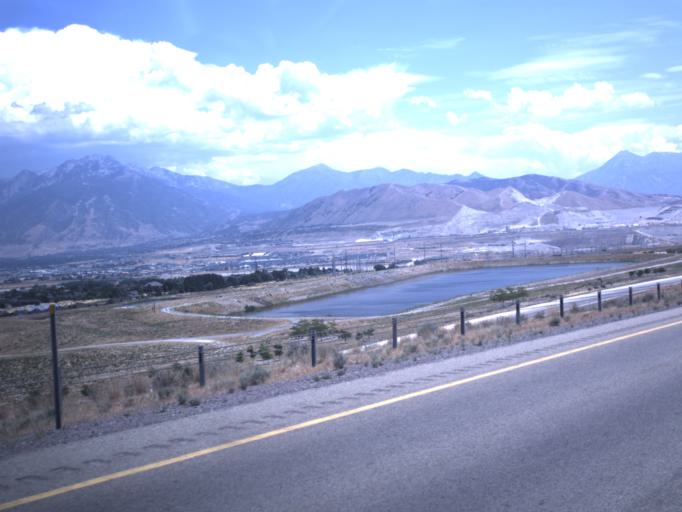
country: US
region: Utah
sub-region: Salt Lake County
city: Bluffdale
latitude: 40.4700
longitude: -111.9681
